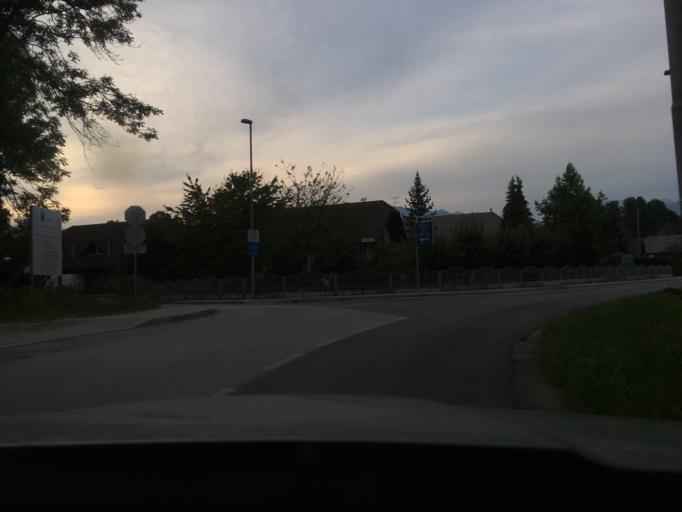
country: SI
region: Kamnik
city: Smarca
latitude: 46.1979
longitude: 14.6005
